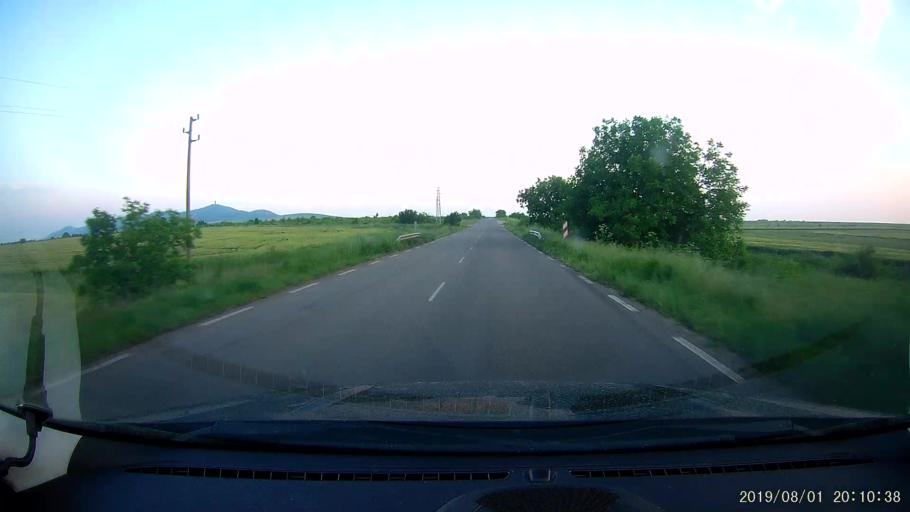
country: BG
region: Yambol
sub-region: Obshtina Yambol
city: Yambol
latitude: 42.4778
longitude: 26.6011
